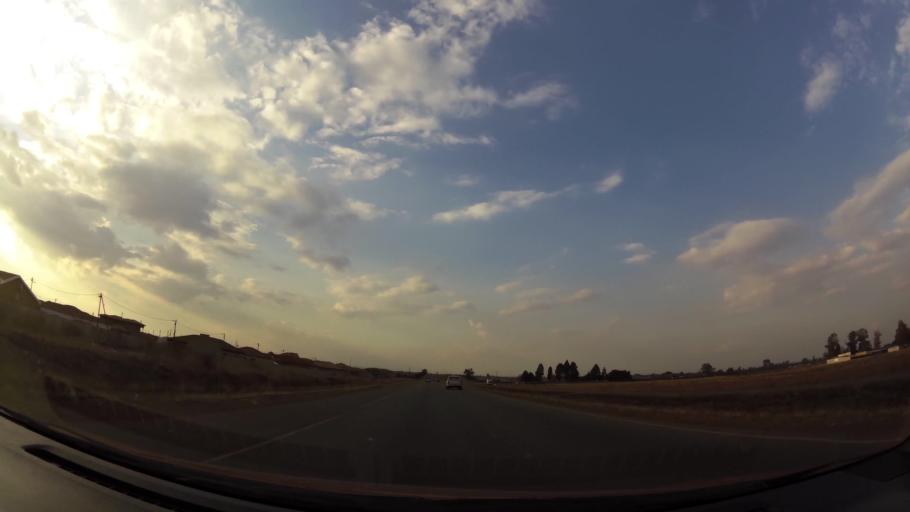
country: ZA
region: Gauteng
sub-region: Sedibeng District Municipality
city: Vanderbijlpark
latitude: -26.6124
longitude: 27.8150
